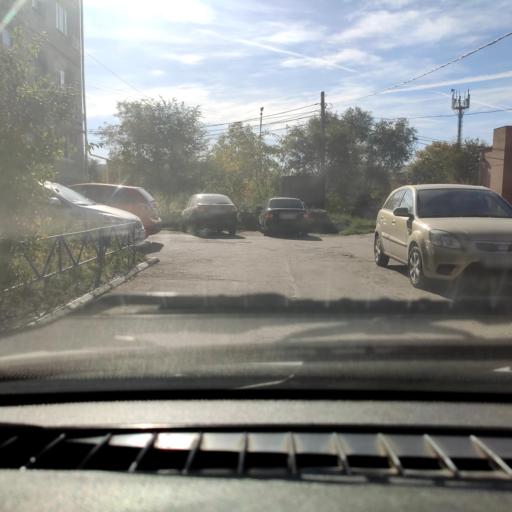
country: RU
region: Samara
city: Zhigulevsk
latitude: 53.4758
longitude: 49.4758
